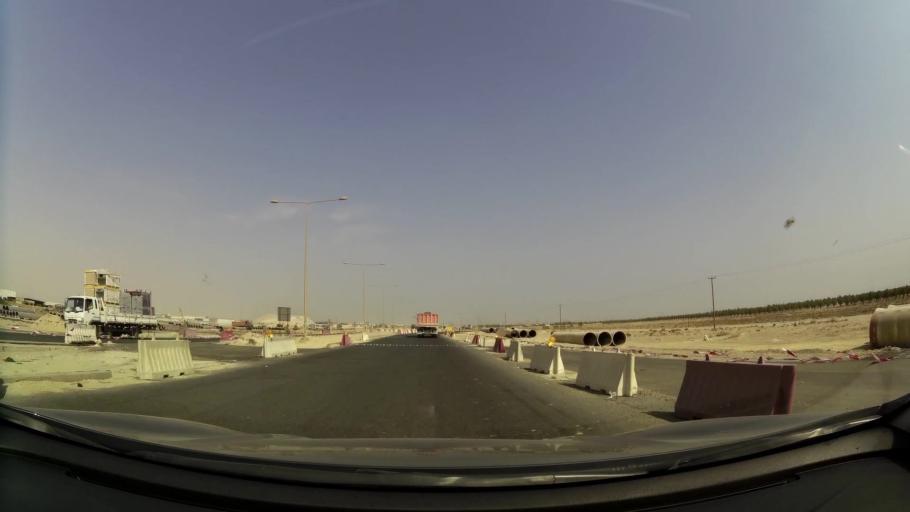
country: KW
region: Al Ahmadi
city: Al Fahahil
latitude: 28.9666
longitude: 48.1259
